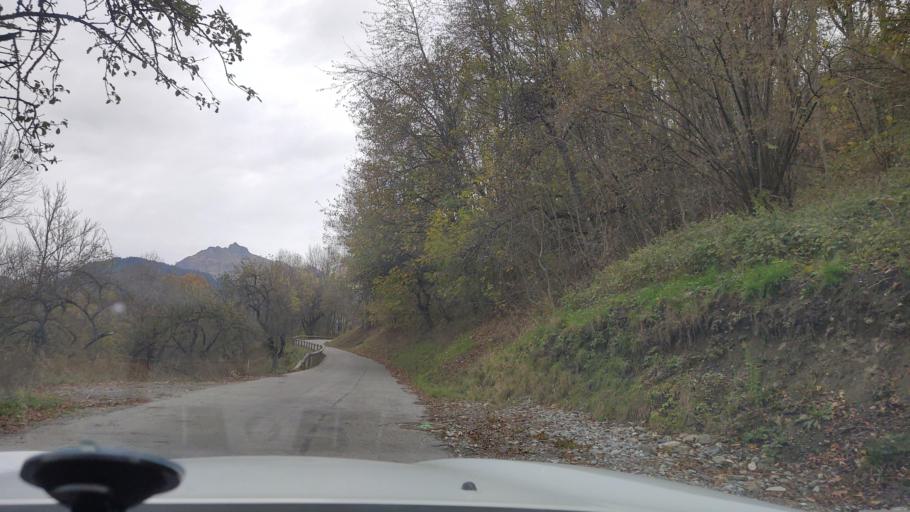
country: FR
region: Rhone-Alpes
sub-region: Departement de la Savoie
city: Bourg-Saint-Maurice
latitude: 45.6064
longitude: 6.7757
